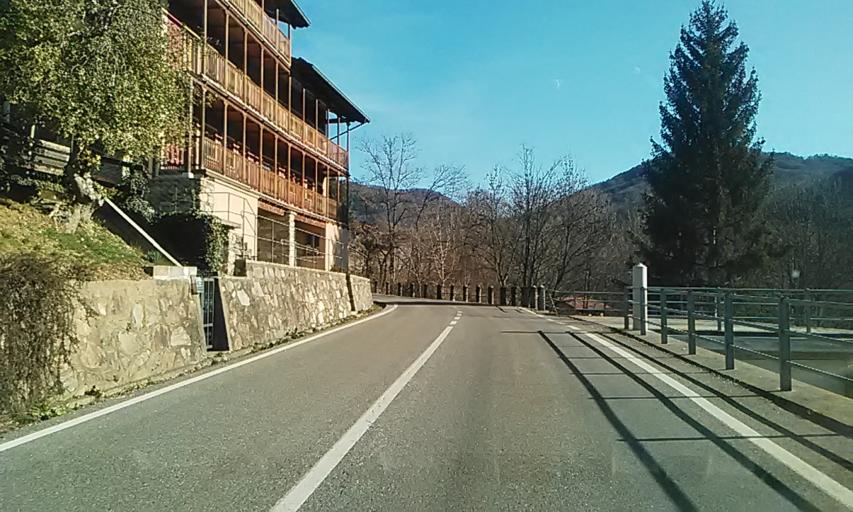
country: IT
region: Piedmont
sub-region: Provincia di Vercelli
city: Civiasco
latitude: 45.8096
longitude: 8.3005
